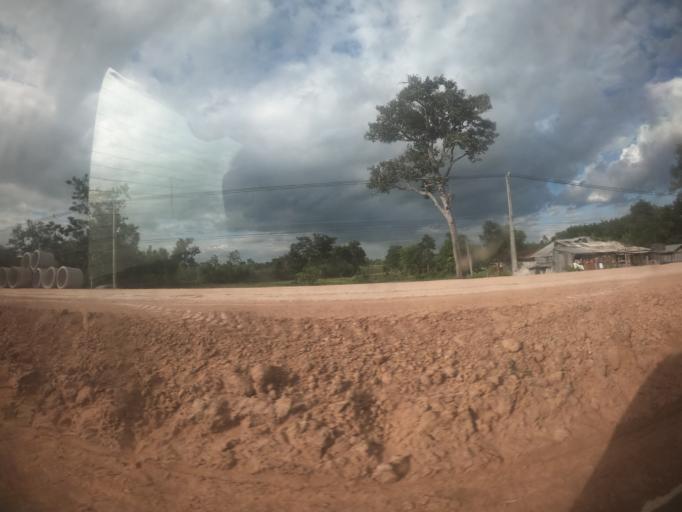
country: TH
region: Surin
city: Kap Choeng
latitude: 14.4957
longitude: 103.5687
